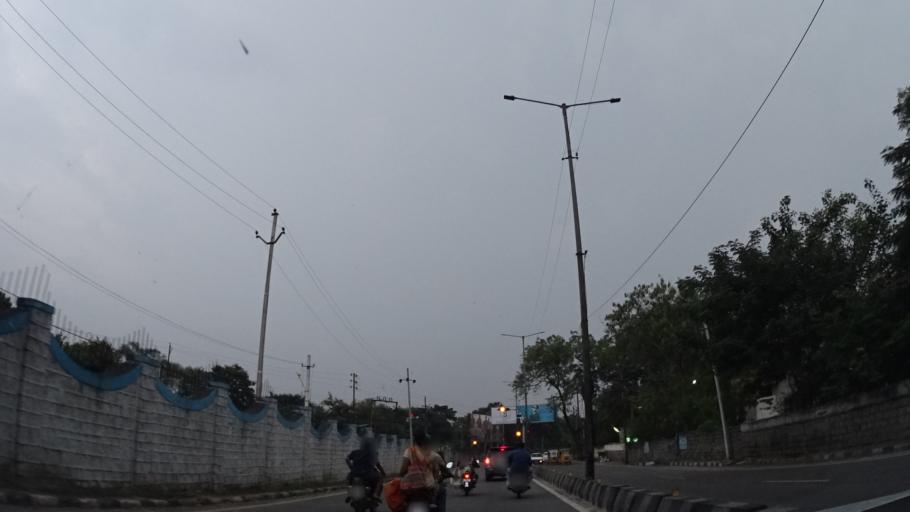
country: IN
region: Telangana
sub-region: Hyderabad
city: Malkajgiri
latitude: 17.4499
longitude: 78.4871
